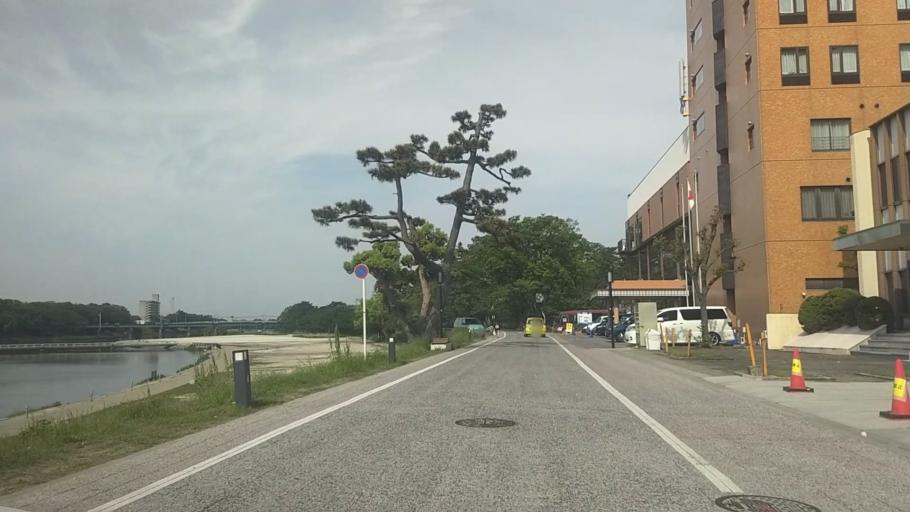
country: JP
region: Aichi
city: Okazaki
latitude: 34.9557
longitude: 137.1621
